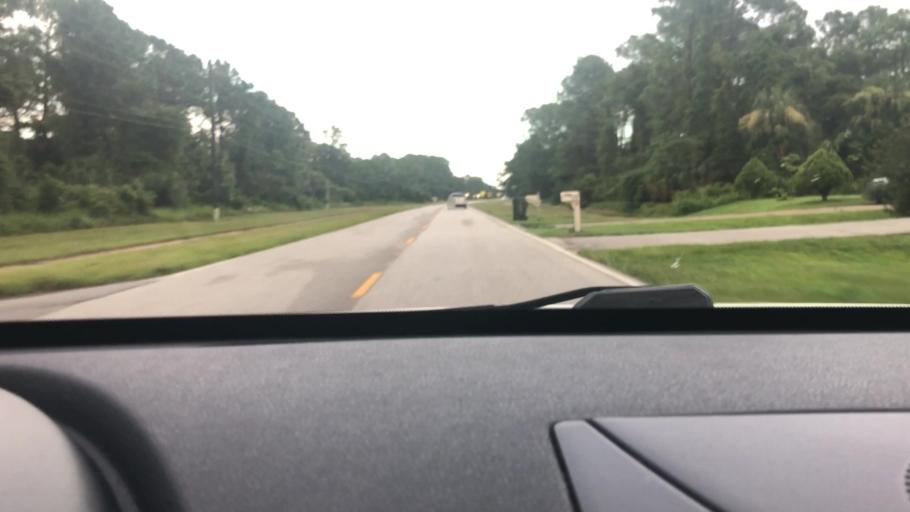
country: US
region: Florida
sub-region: Sarasota County
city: North Port
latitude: 27.0689
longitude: -82.1371
